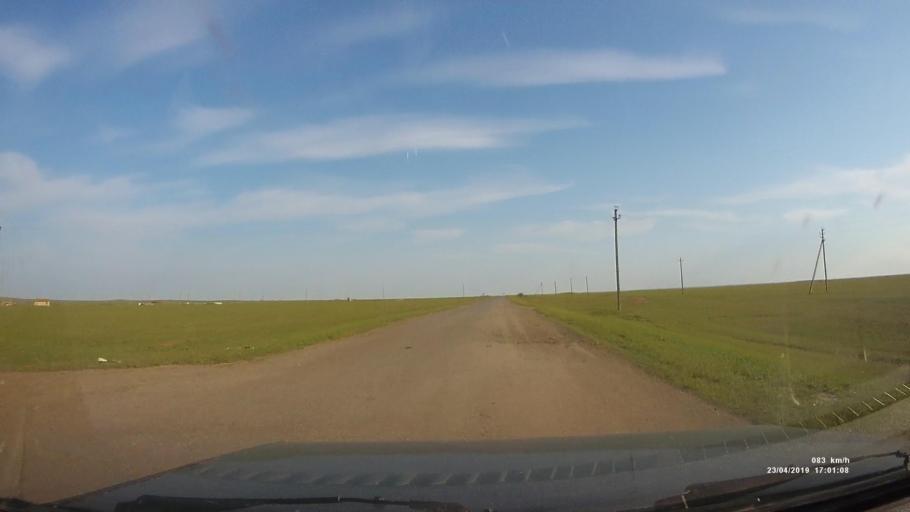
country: RU
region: Kalmykiya
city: Priyutnoye
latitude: 46.2993
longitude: 43.4071
